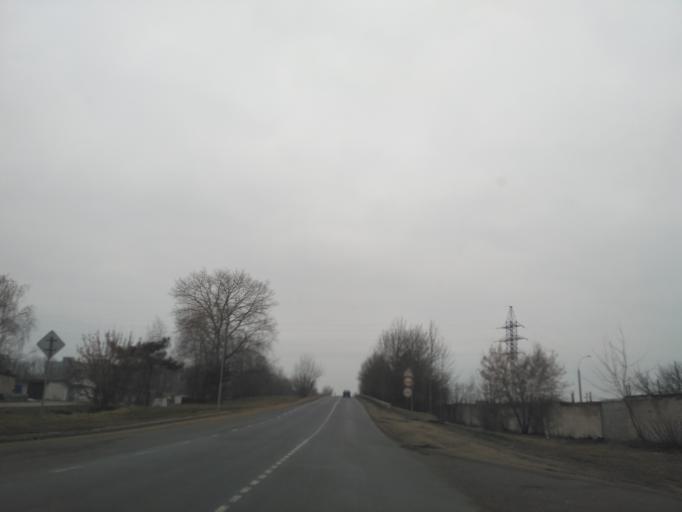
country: BY
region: Brest
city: Baranovichi
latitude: 53.1613
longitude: 26.0122
